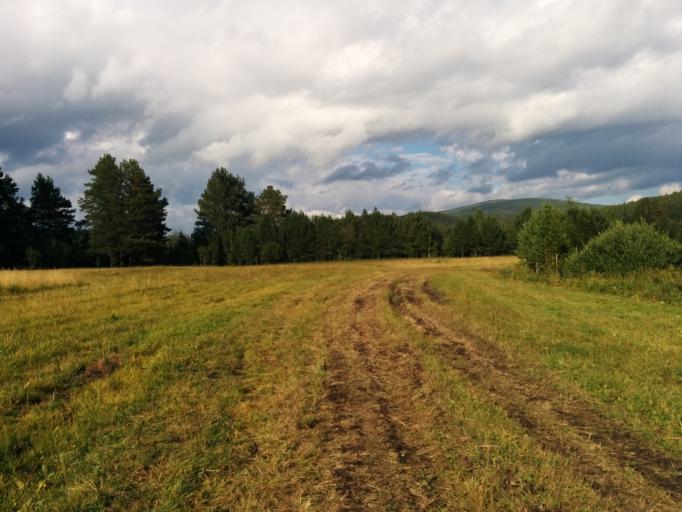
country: RU
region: Bashkortostan
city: Beloretsk
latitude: 54.0450
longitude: 58.3239
